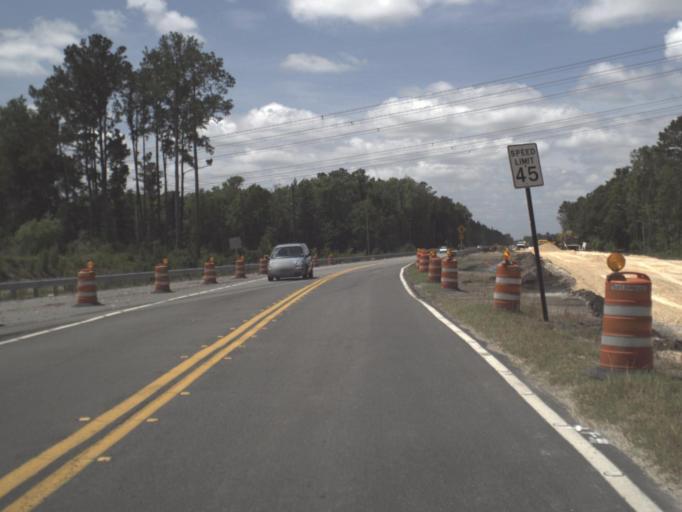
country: US
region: Florida
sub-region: Duval County
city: Baldwin
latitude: 30.3804
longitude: -81.9404
